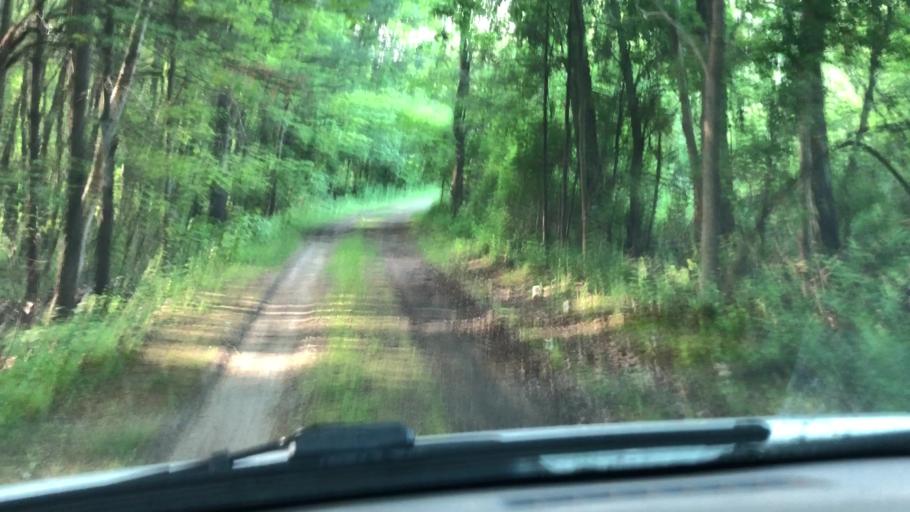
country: US
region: Massachusetts
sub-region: Hampshire County
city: Northampton
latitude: 42.3049
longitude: -72.6606
